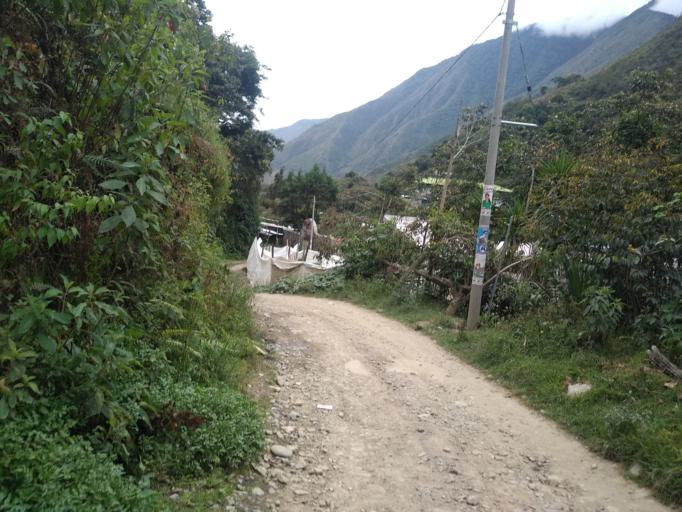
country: PE
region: Cusco
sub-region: Provincia de La Convencion
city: Santa Teresa
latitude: -13.2271
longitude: -72.6287
